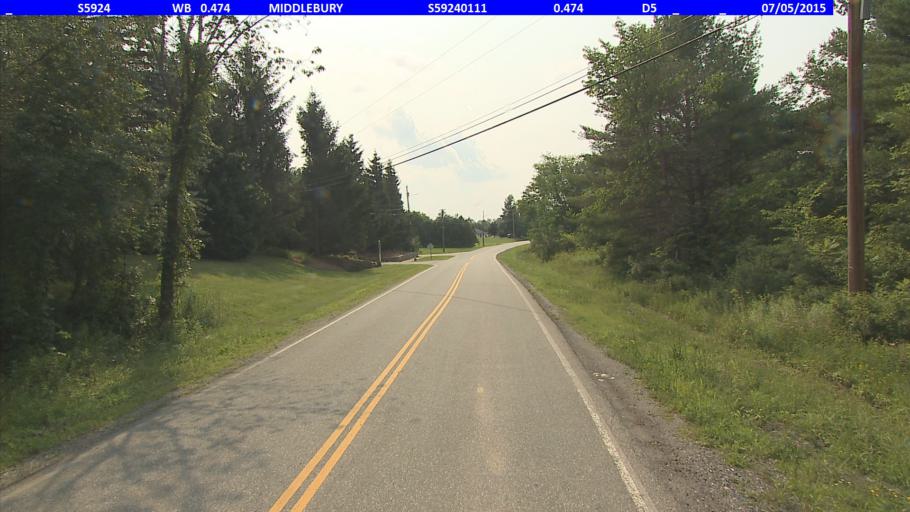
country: US
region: Vermont
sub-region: Addison County
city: Middlebury (village)
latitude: 44.0156
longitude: -73.1518
